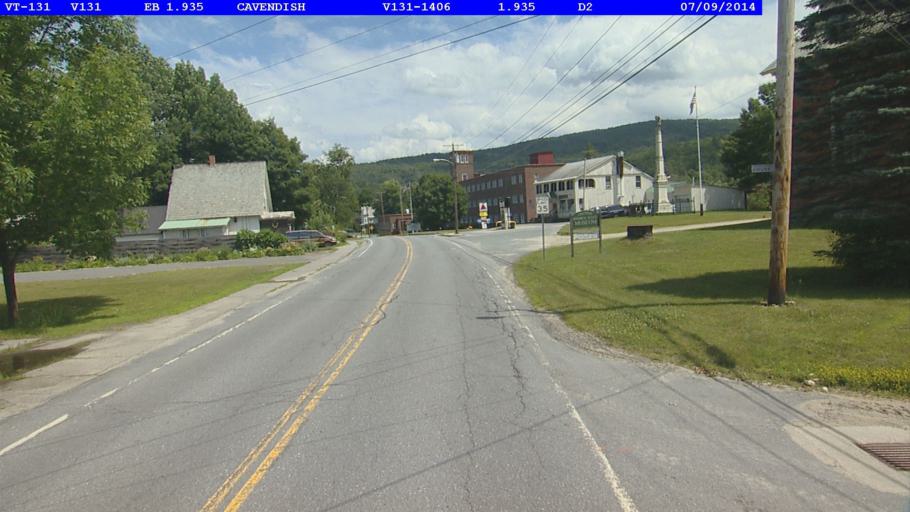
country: US
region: Vermont
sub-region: Windsor County
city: Chester
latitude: 43.3824
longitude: -72.6113
